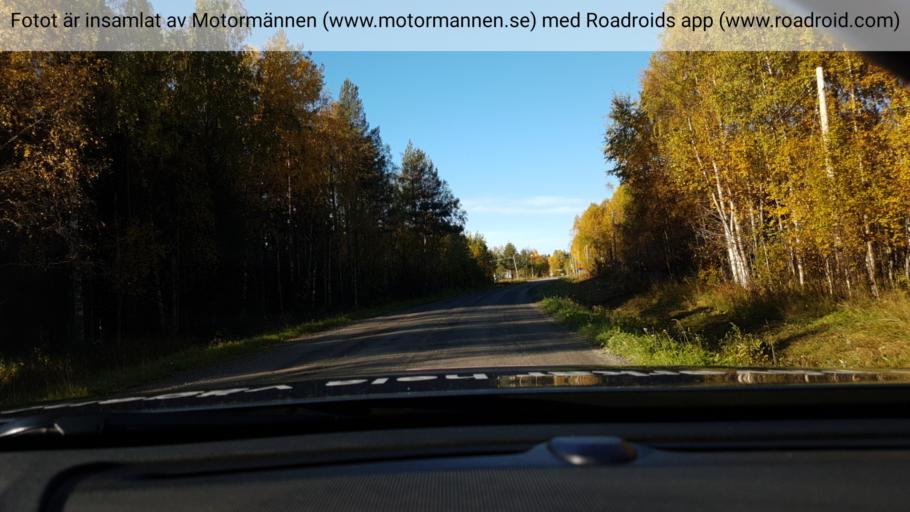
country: SE
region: Norrbotten
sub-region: Alvsbyns Kommun
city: AElvsbyn
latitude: 66.2799
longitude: 21.1323
